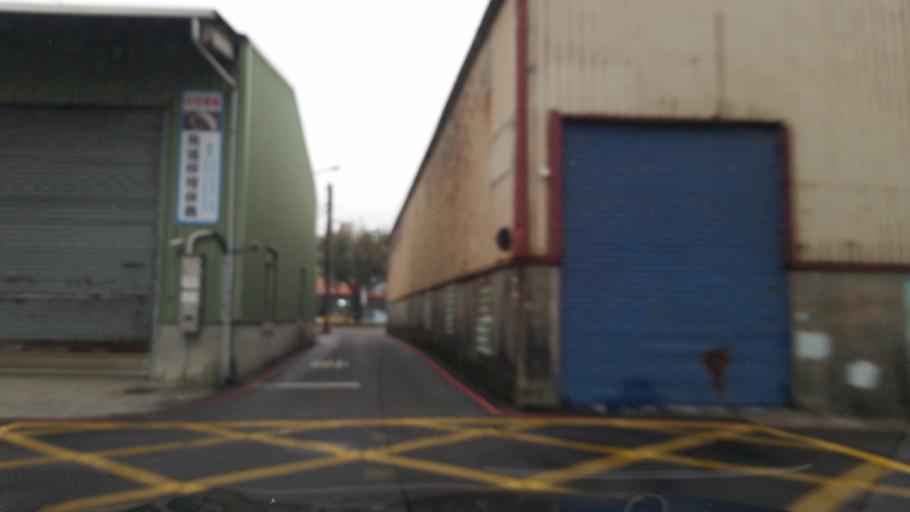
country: TW
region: Taiwan
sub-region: Taoyuan
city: Taoyuan
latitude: 25.0552
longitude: 121.3601
